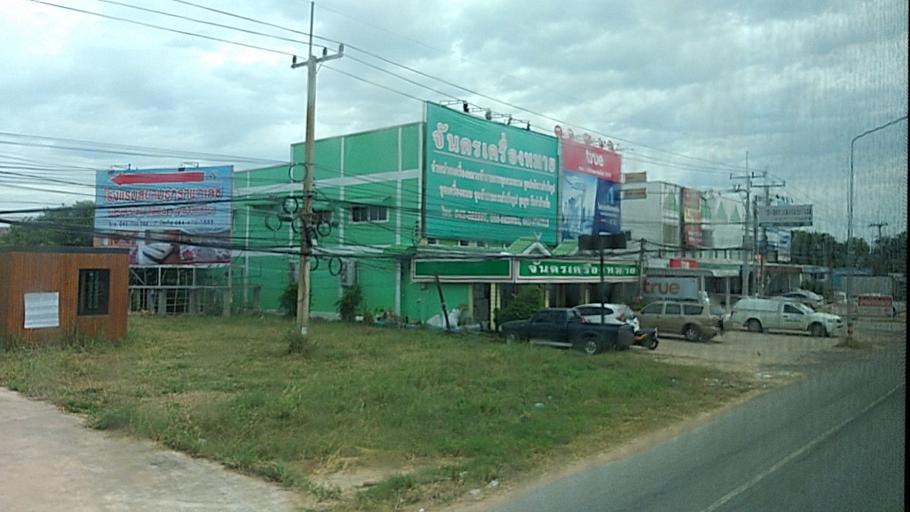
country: TH
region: Maha Sarakham
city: Maha Sarakham
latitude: 16.2125
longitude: 103.2810
